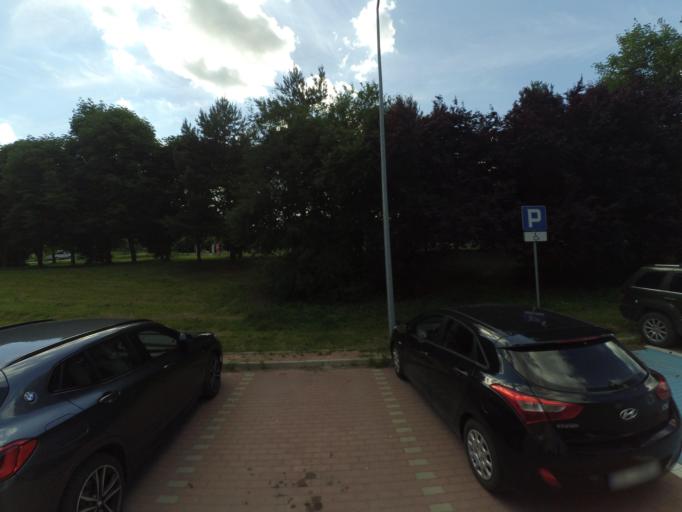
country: PL
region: Lower Silesian Voivodeship
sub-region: Powiat klodzki
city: Klodzko
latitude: 50.4344
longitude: 16.6439
